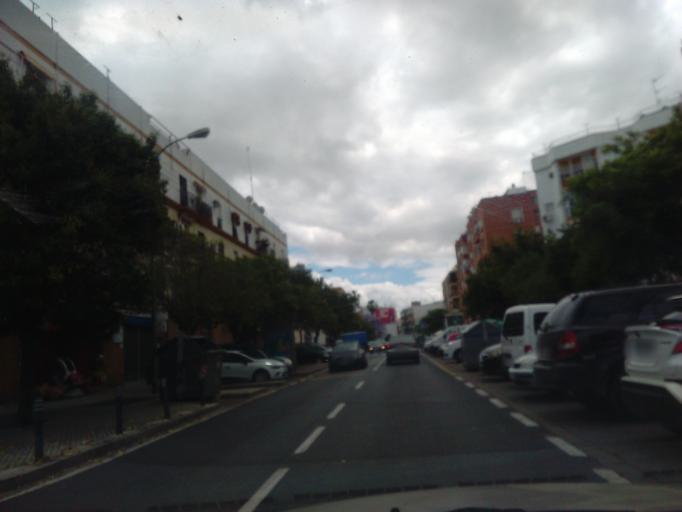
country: ES
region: Andalusia
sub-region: Provincia de Sevilla
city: Sevilla
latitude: 37.3725
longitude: -5.9524
